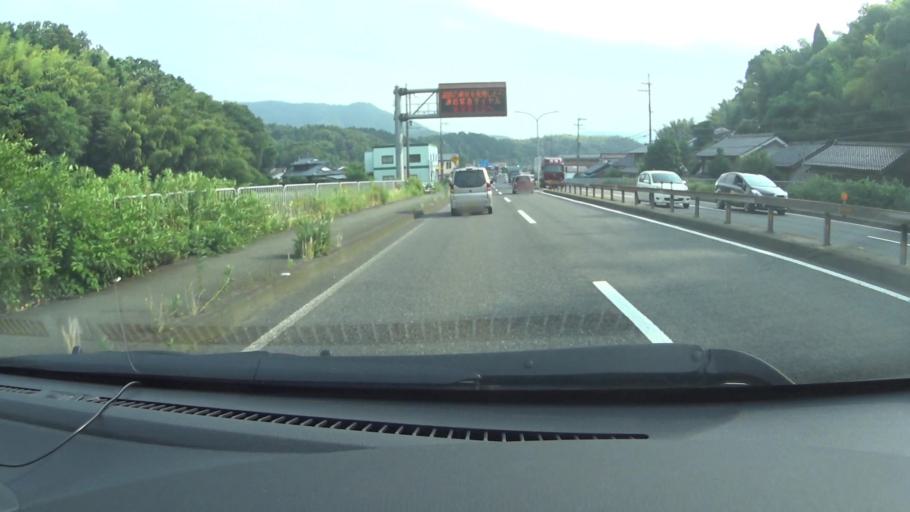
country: JP
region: Kyoto
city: Maizuru
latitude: 35.4547
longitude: 135.3494
